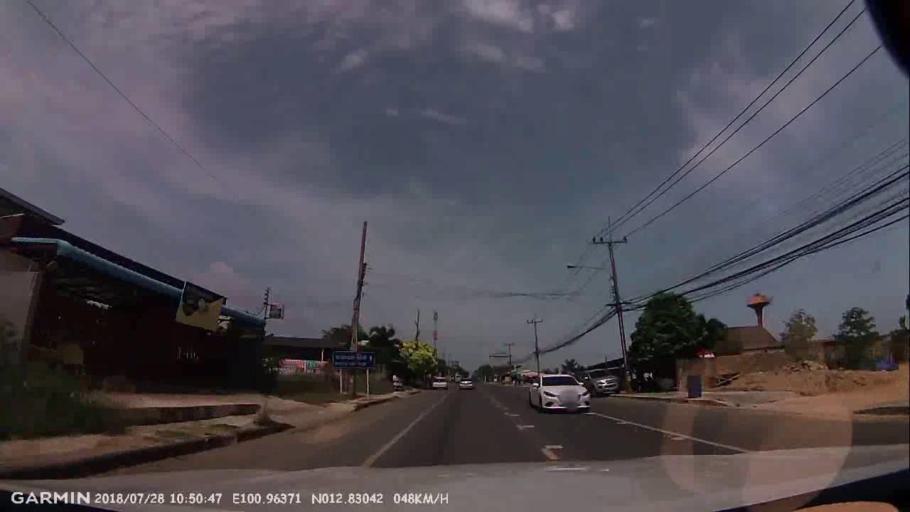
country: TH
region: Chon Buri
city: Phatthaya
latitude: 12.8304
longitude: 100.9636
